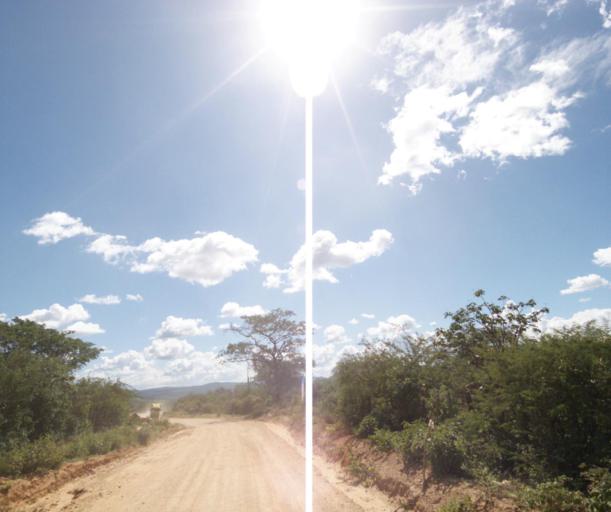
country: BR
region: Bahia
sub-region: Pocoes
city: Pocoes
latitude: -14.2525
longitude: -40.7109
